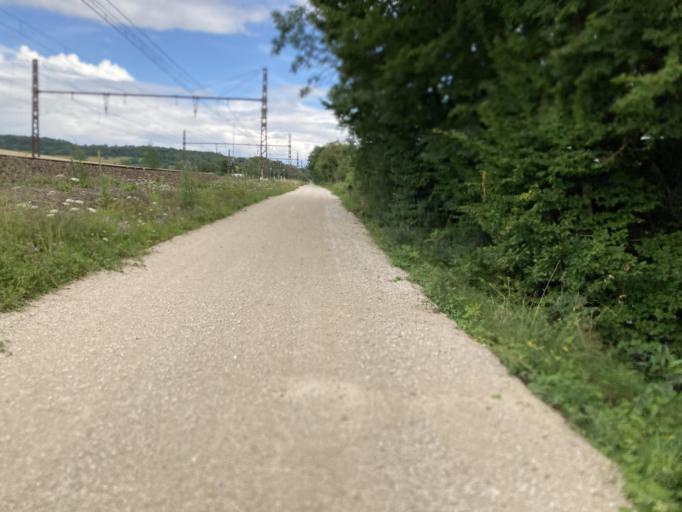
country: FR
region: Bourgogne
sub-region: Departement de la Cote-d'Or
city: Montbard
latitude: 47.6157
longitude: 4.3788
